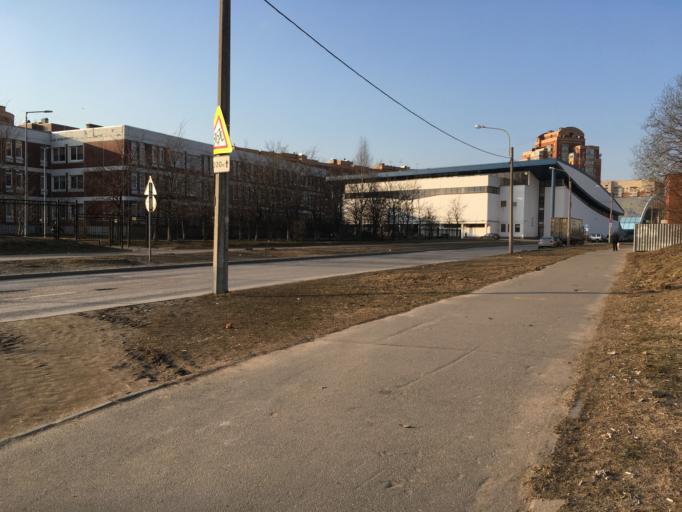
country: RU
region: St.-Petersburg
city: Komendantsky aerodrom
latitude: 60.0011
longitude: 30.2617
